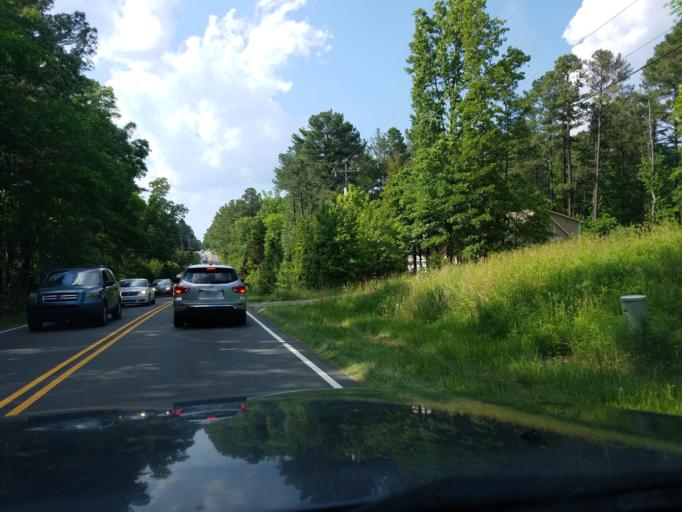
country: US
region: North Carolina
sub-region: Durham County
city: Durham
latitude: 35.9383
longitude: -78.9639
